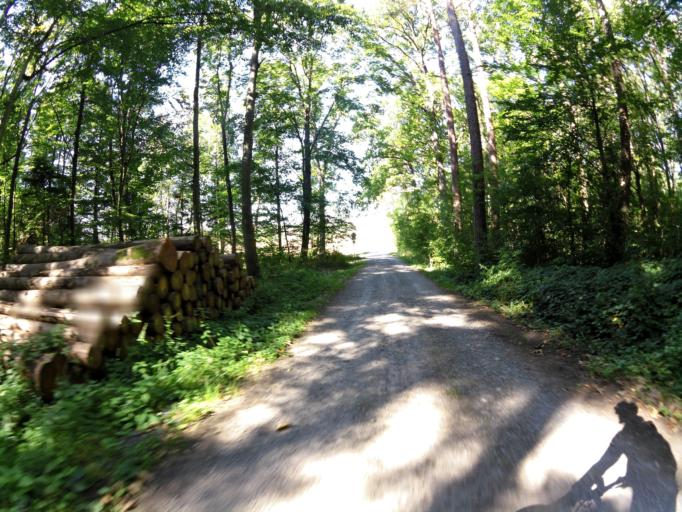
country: DE
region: Bavaria
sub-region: Regierungsbezirk Unterfranken
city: Kleinrinderfeld
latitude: 49.6981
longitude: 9.8037
